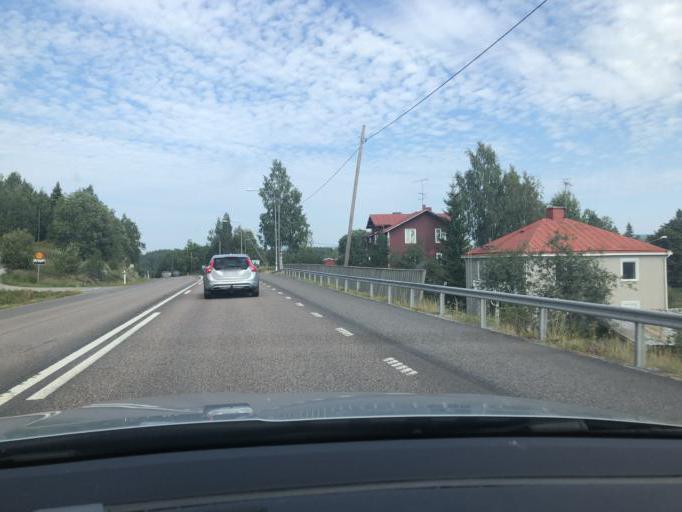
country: SE
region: Vaesternorrland
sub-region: Kramfors Kommun
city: Kramfors
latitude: 62.8886
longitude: 17.8525
